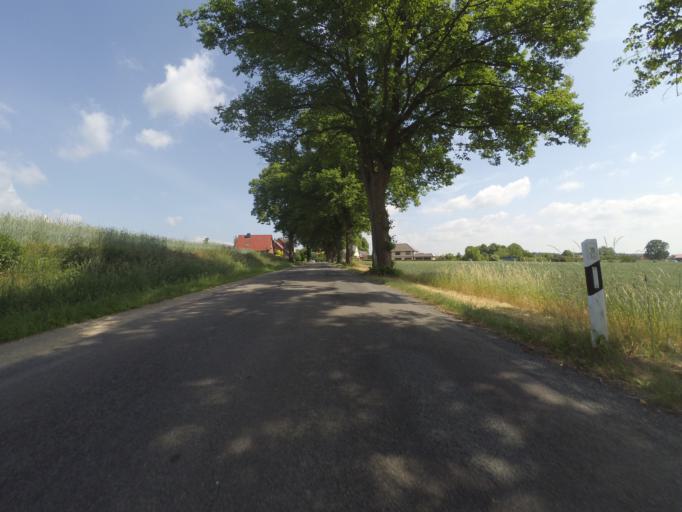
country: DE
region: Mecklenburg-Vorpommern
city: Lubz
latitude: 53.4430
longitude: 12.0797
